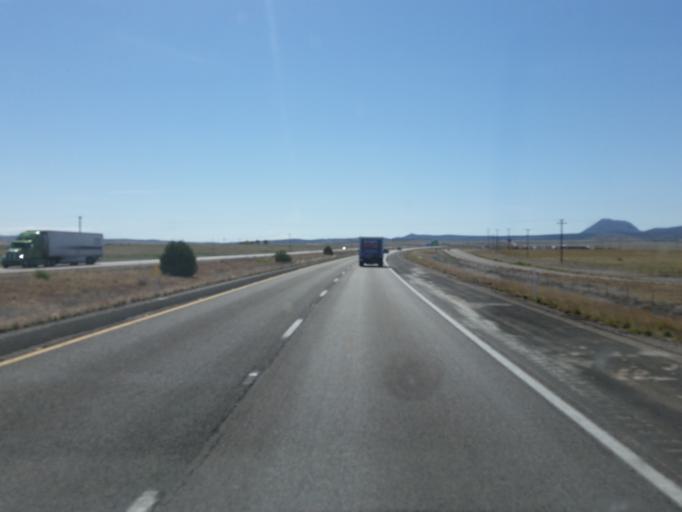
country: US
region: Arizona
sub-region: Yavapai County
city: Paulden
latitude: 35.3144
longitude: -112.8649
